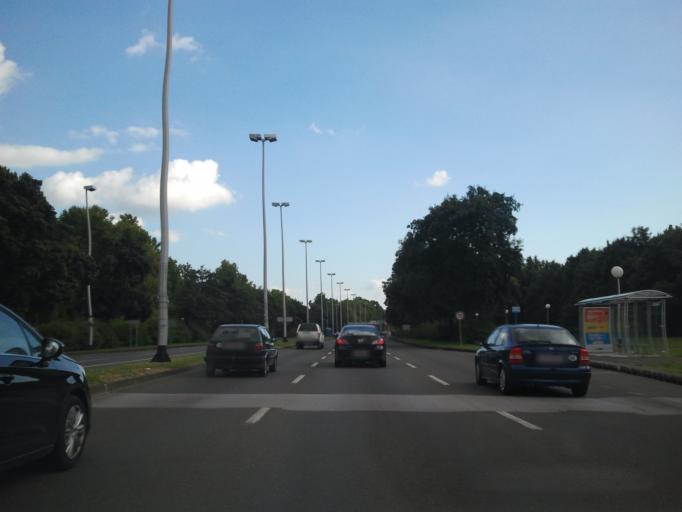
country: HR
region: Grad Zagreb
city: Novi Zagreb
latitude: 45.7674
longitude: 15.9909
